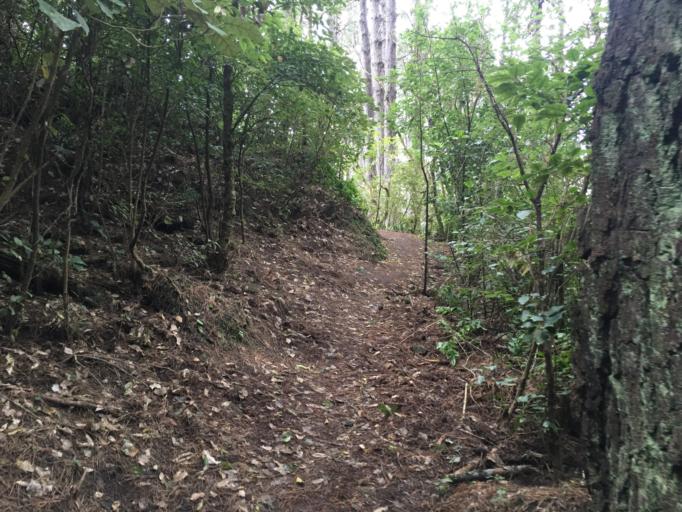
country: NZ
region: Wellington
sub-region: Wellington City
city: Kelburn
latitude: -41.2720
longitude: 174.7715
